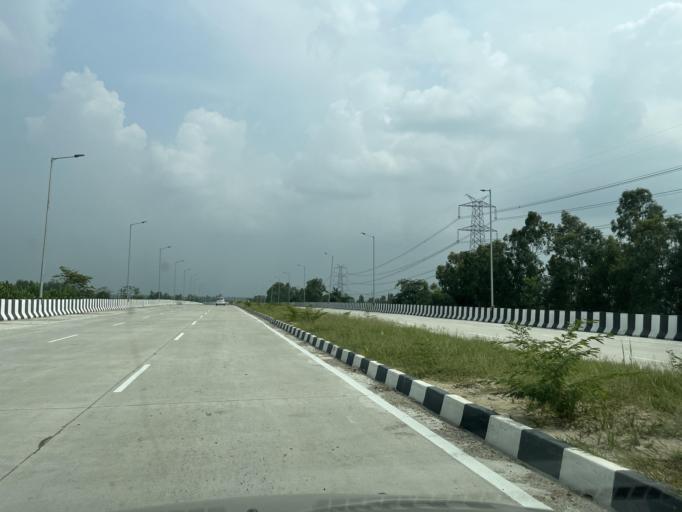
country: IN
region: Uttarakhand
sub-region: Udham Singh Nagar
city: Jaspur
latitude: 29.2953
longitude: 78.8416
